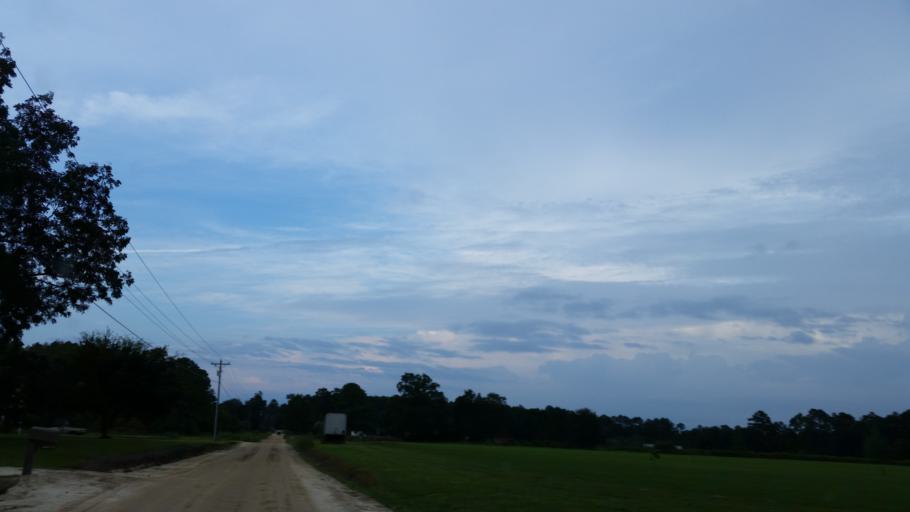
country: US
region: Georgia
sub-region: Lowndes County
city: Valdosta
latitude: 30.7217
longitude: -83.2990
